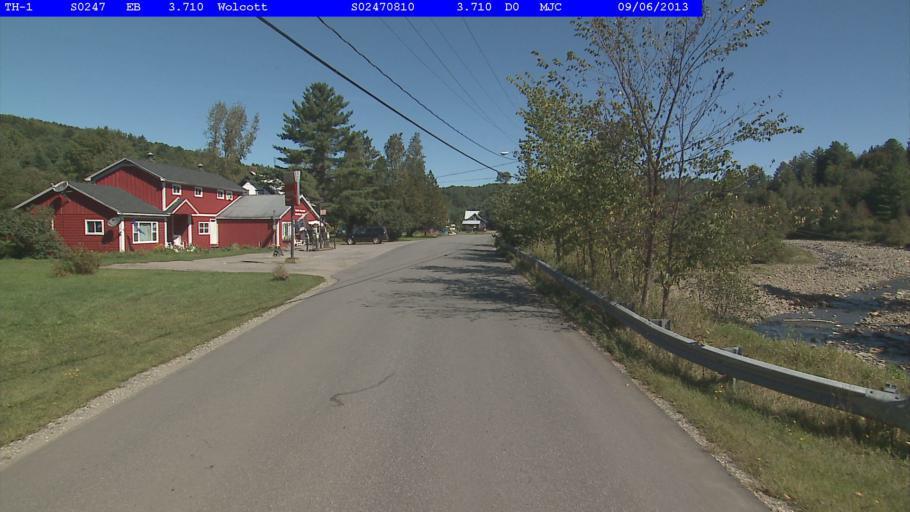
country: US
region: Vermont
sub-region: Caledonia County
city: Hardwick
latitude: 44.6066
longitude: -72.4646
